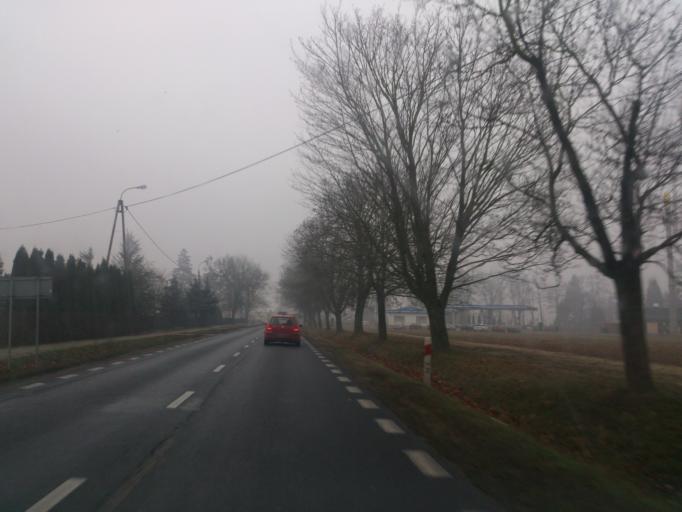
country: PL
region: Masovian Voivodeship
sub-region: Powiat sierpecki
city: Sierpc
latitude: 52.8664
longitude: 19.6637
